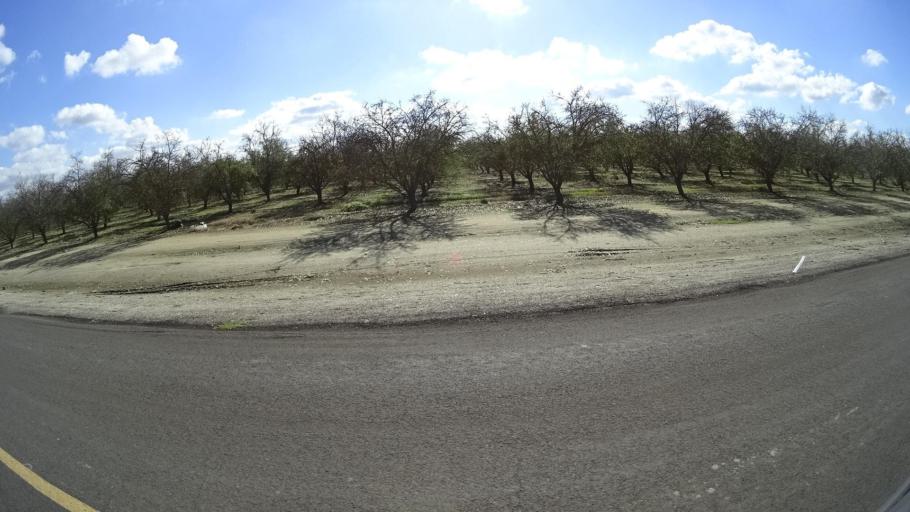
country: US
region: California
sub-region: Kern County
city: Delano
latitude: 35.7322
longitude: -119.3094
